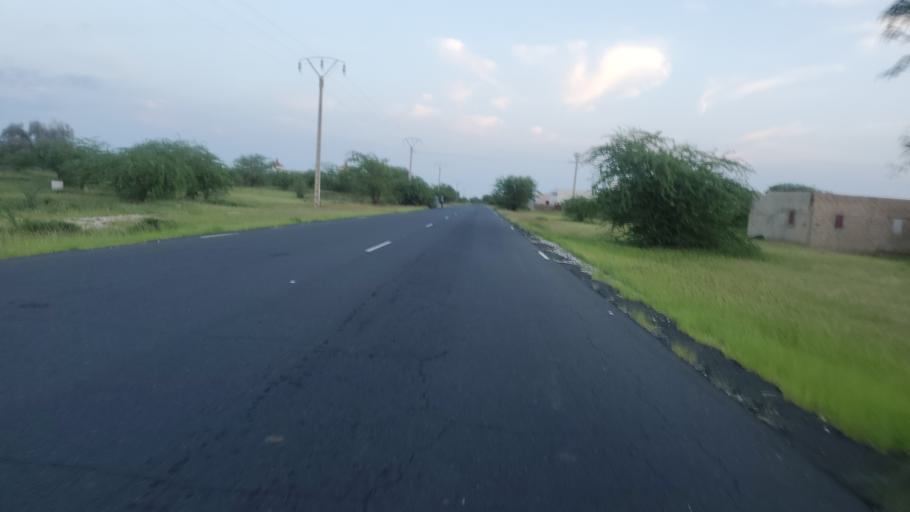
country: SN
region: Saint-Louis
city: Saint-Louis
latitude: 16.1081
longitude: -16.4123
